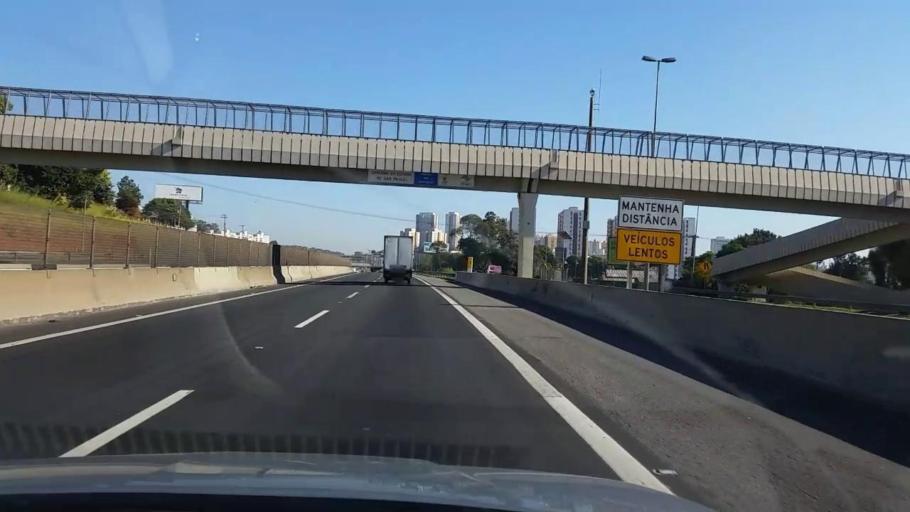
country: BR
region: Sao Paulo
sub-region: Jundiai
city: Jundiai
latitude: -23.2157
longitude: -46.8845
